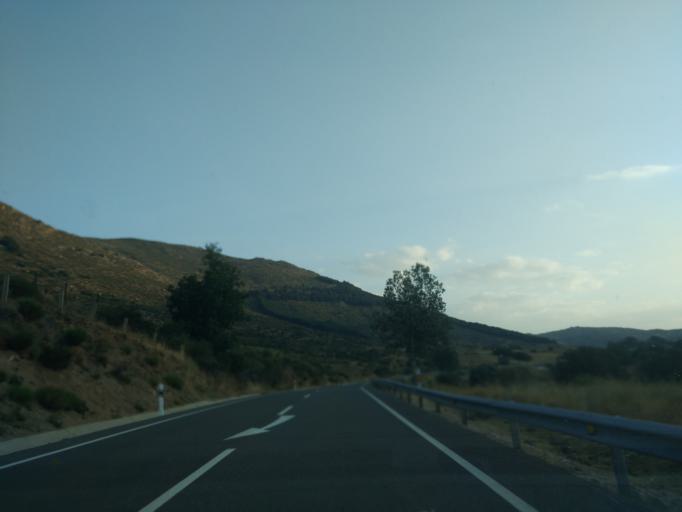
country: ES
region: Castille and Leon
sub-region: Provincia de Avila
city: Mengamunoz
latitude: 40.5056
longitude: -4.9930
